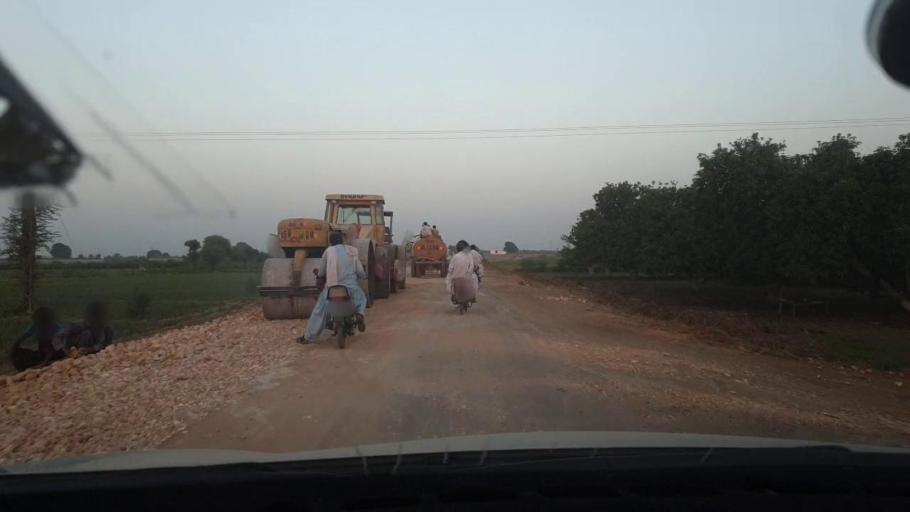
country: PK
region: Sindh
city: Bhit Shah
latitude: 25.7528
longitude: 68.5422
